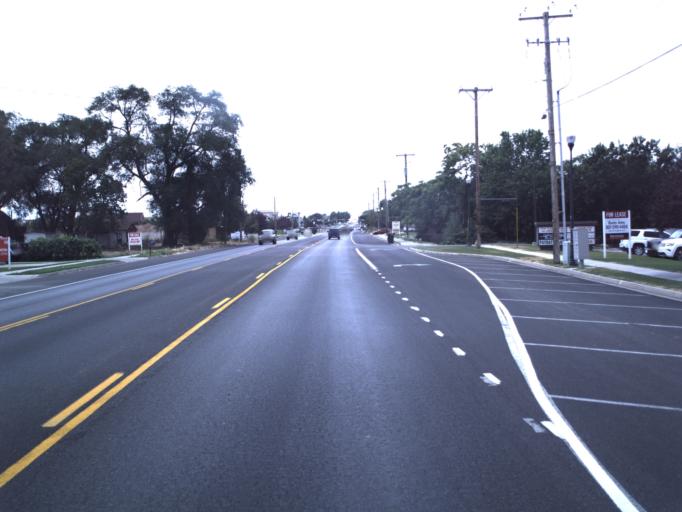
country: US
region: Utah
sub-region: Davis County
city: Clinton
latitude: 41.1456
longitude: -112.0645
